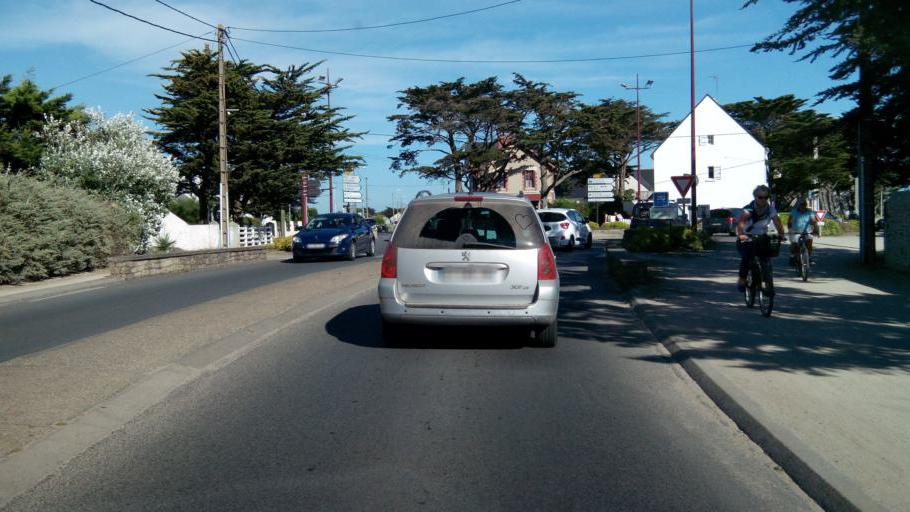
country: FR
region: Pays de la Loire
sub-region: Departement de la Loire-Atlantique
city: Batz-sur-Mer
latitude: 47.2813
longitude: -2.4968
